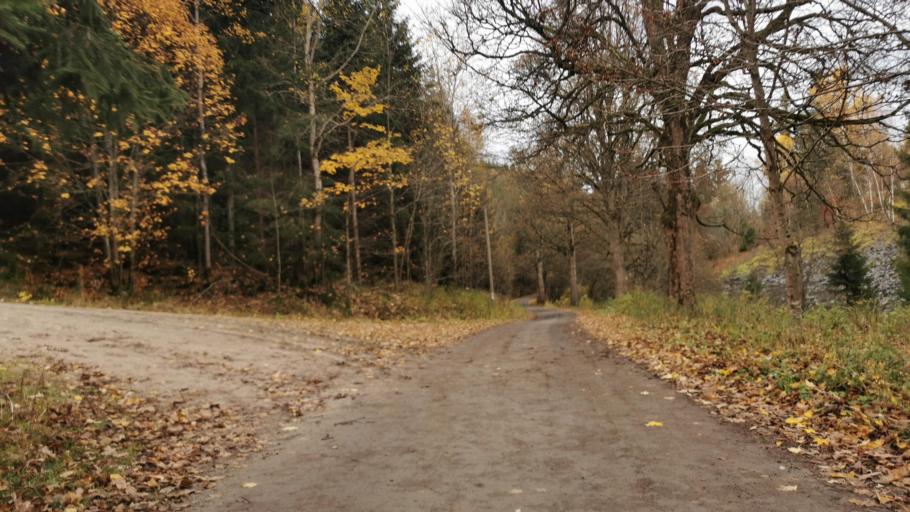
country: DE
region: Thuringia
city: Wurzbach
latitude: 50.4464
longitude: 11.5499
